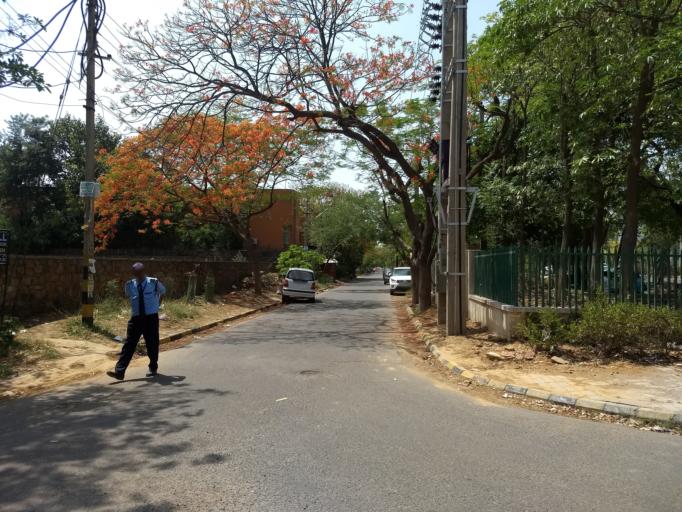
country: IN
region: Haryana
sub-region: Gurgaon
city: Gurgaon
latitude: 28.4597
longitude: 77.0690
